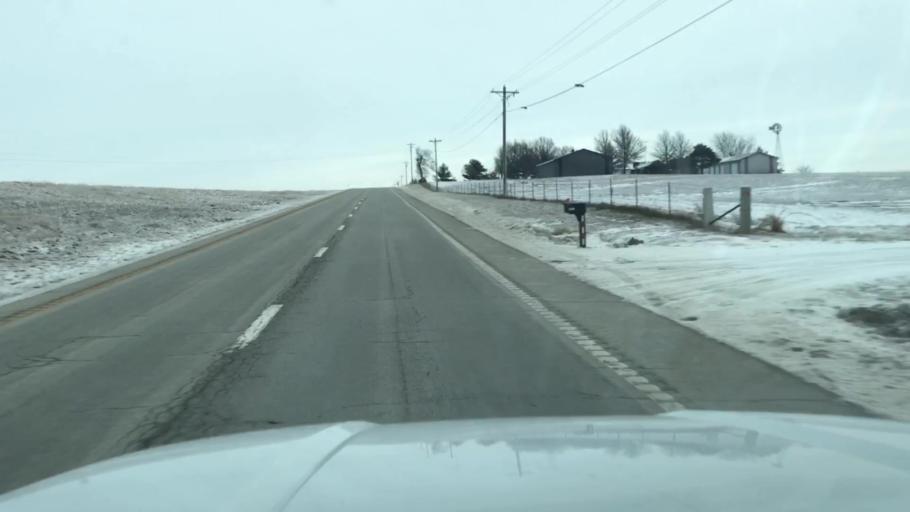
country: US
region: Missouri
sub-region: Andrew County
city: Savannah
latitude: 39.9904
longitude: -94.8799
